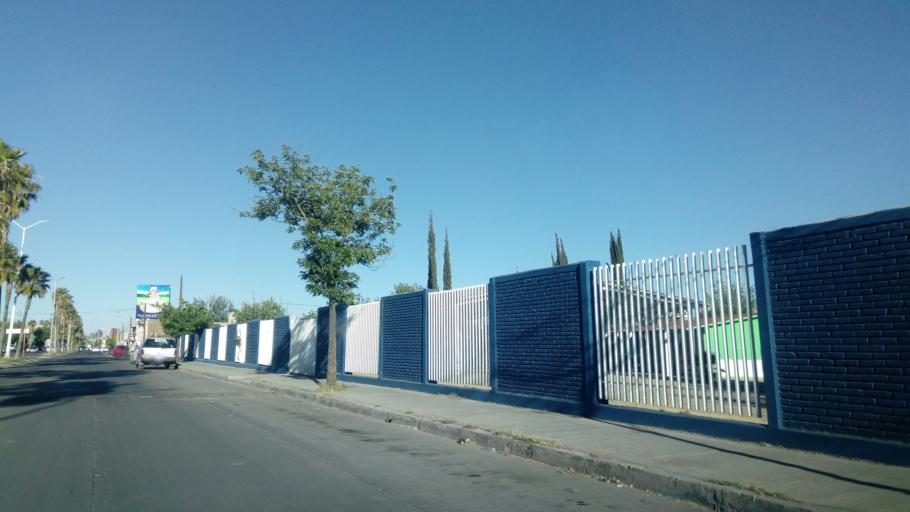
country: MX
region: Durango
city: Victoria de Durango
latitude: 24.0108
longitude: -104.6891
